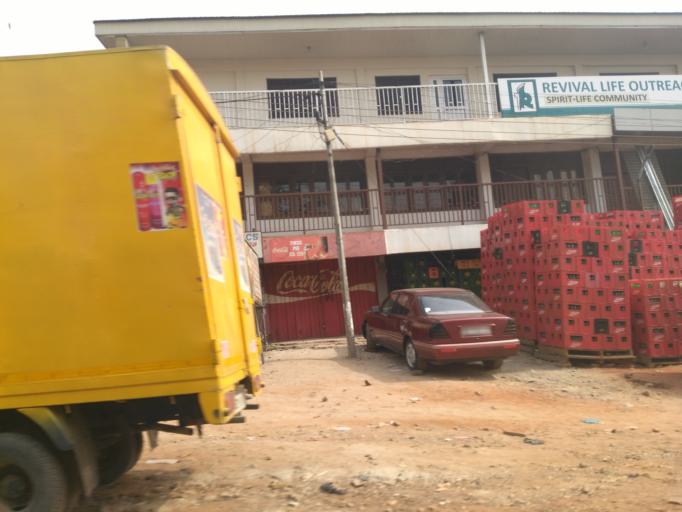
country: GH
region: Ashanti
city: Kumasi
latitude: 6.6597
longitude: -1.5985
